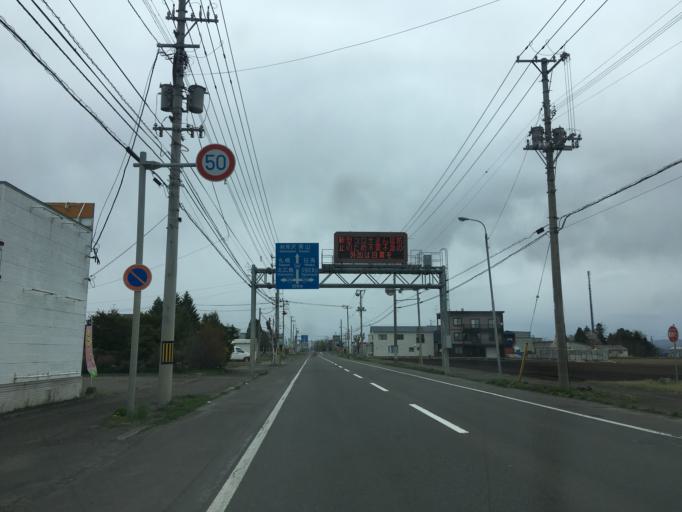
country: JP
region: Hokkaido
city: Chitose
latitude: 42.9470
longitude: 141.8032
